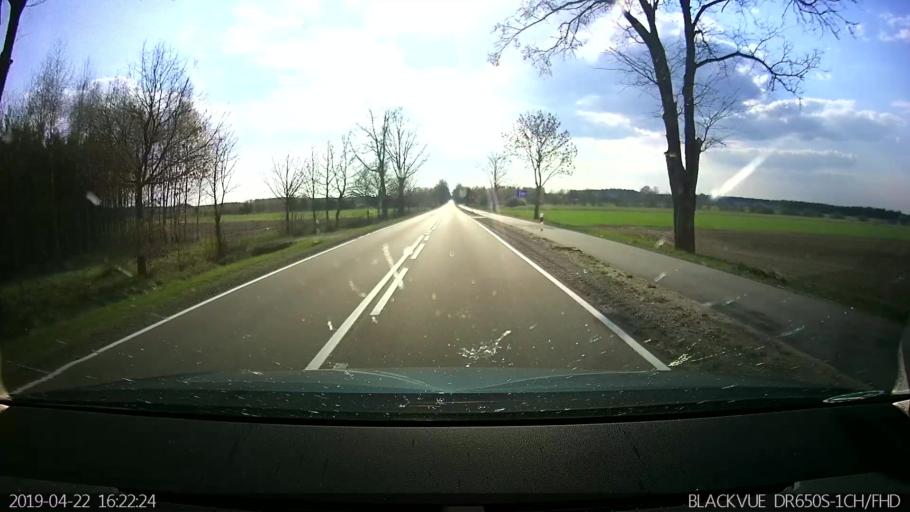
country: PL
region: Podlasie
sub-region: Powiat hajnowski
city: Kleszczele
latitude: 52.5629
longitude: 23.3076
